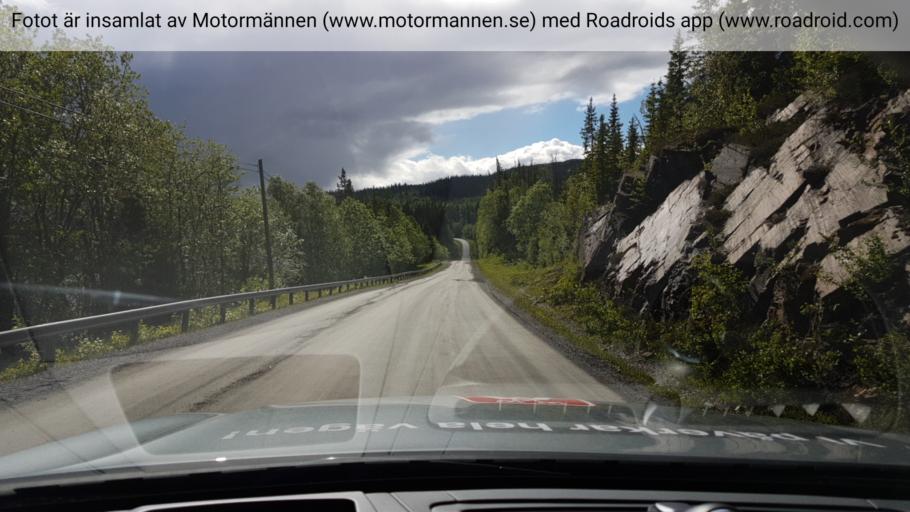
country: SE
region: Jaemtland
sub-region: Are Kommun
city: Are
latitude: 63.6897
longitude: 12.9240
